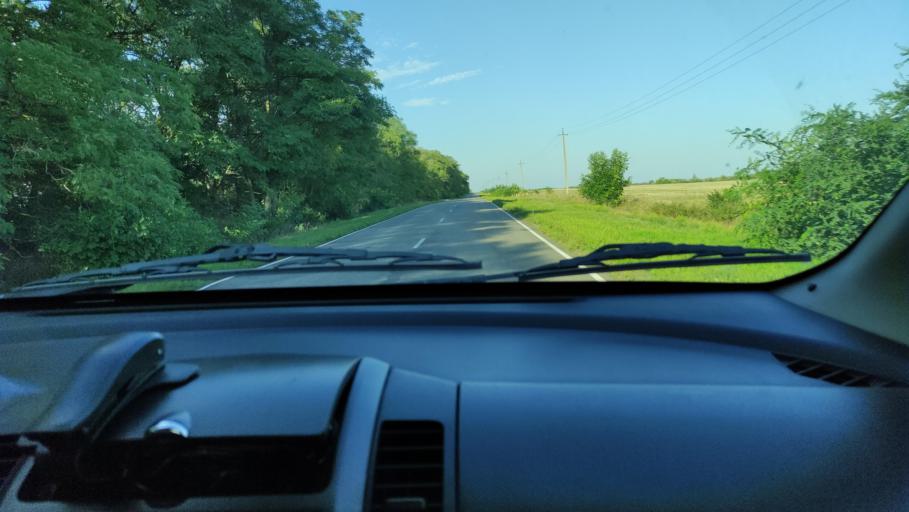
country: RU
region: Voronezj
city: Verkhniy Mamon
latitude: 50.1321
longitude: 40.3269
